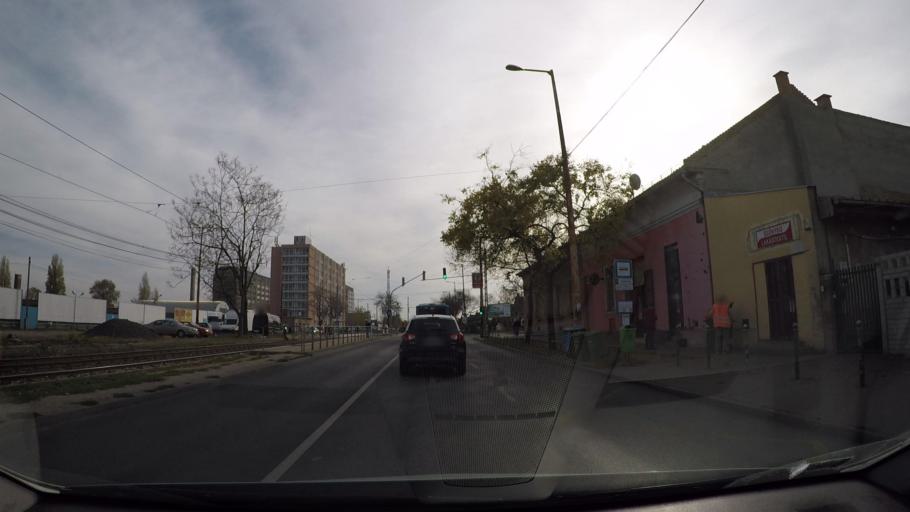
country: HU
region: Budapest
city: Budapest X. keruelet
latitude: 47.4777
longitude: 19.1653
